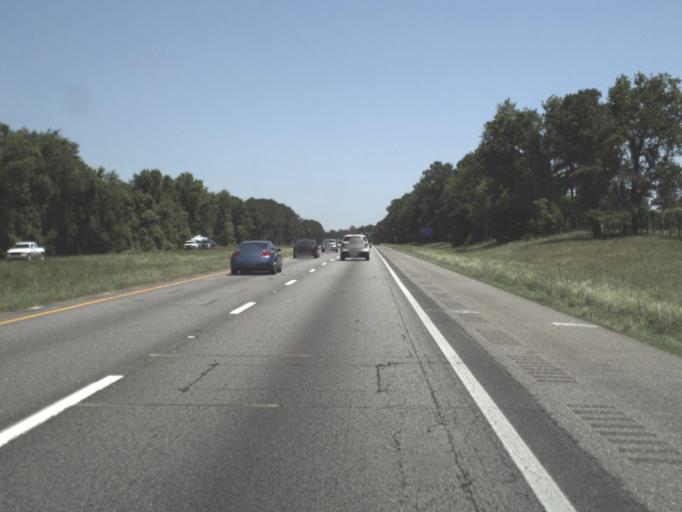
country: US
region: Florida
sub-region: Jefferson County
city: Monticello
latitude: 30.4511
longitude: -83.7535
